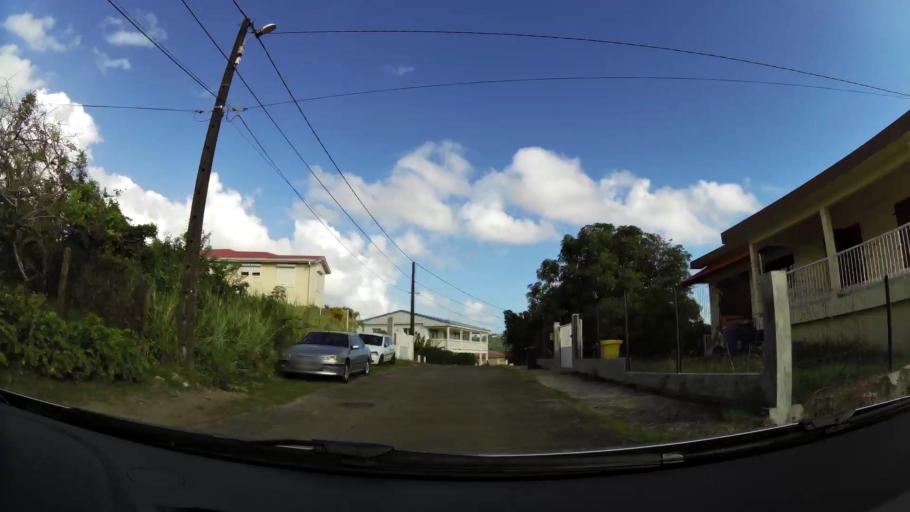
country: MQ
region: Martinique
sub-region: Martinique
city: Le Francois
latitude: 14.6123
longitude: -60.9103
